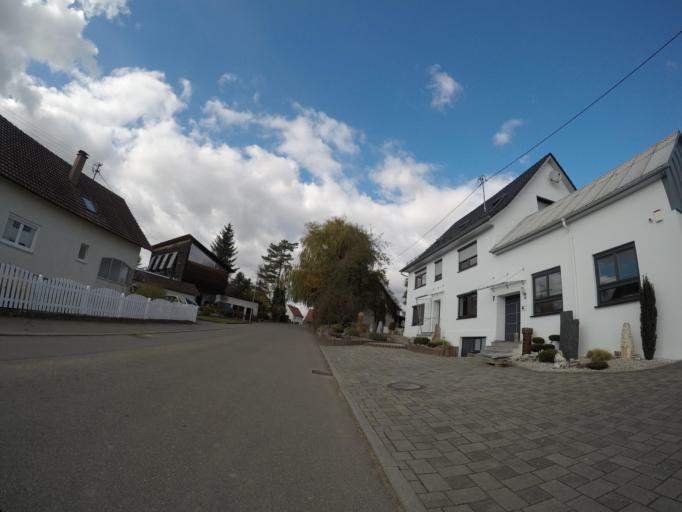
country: DE
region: Baden-Wuerttemberg
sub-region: Tuebingen Region
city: Unterstadion
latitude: 48.2038
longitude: 9.6926
